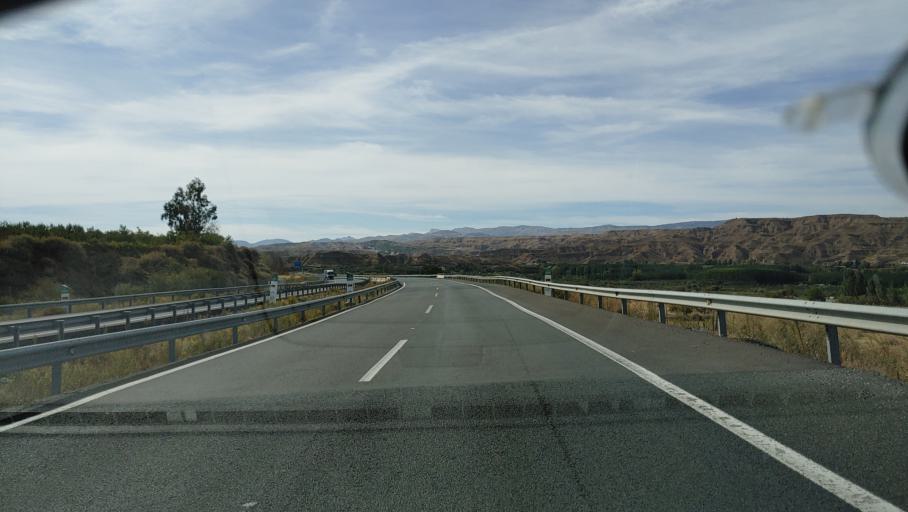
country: ES
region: Andalusia
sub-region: Provincia de Granada
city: Purullena
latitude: 37.3281
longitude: -3.1833
